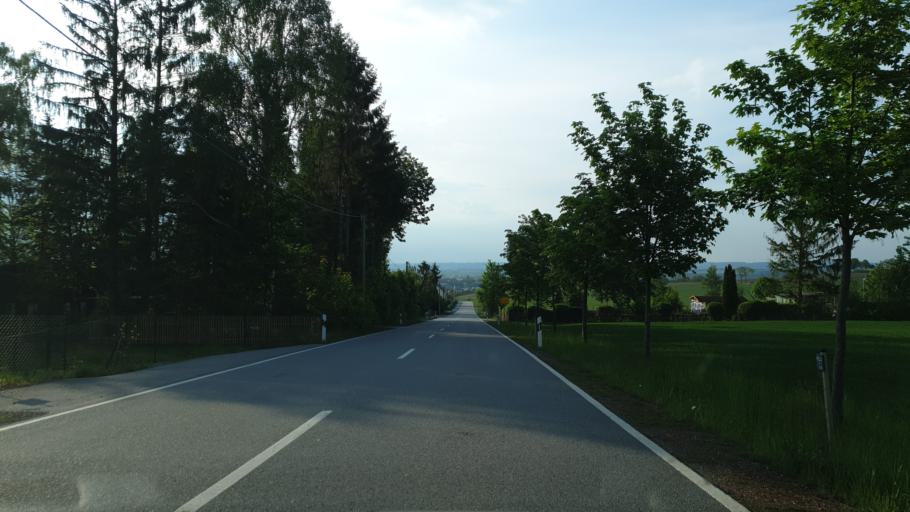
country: DE
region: Saxony
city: Stollberg
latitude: 50.6982
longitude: 12.7933
